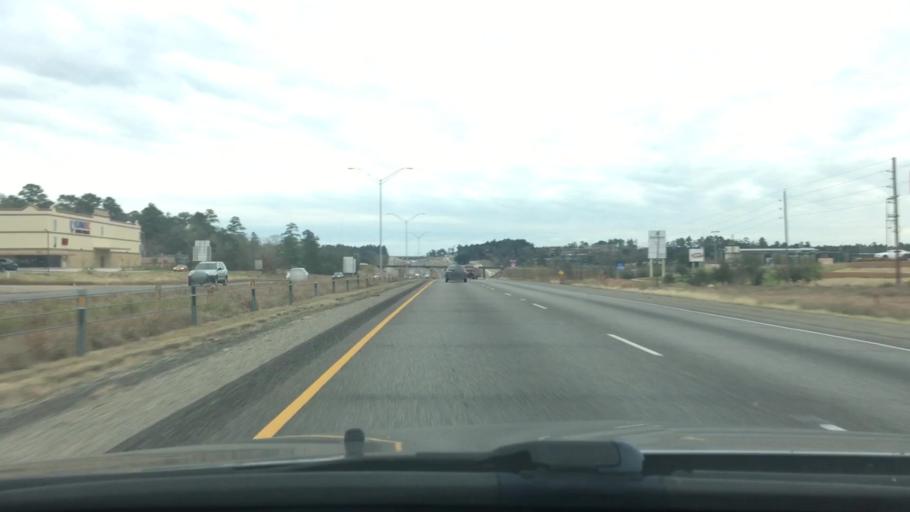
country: US
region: Texas
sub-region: Walker County
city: Huntsville
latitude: 30.7090
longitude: -95.5637
